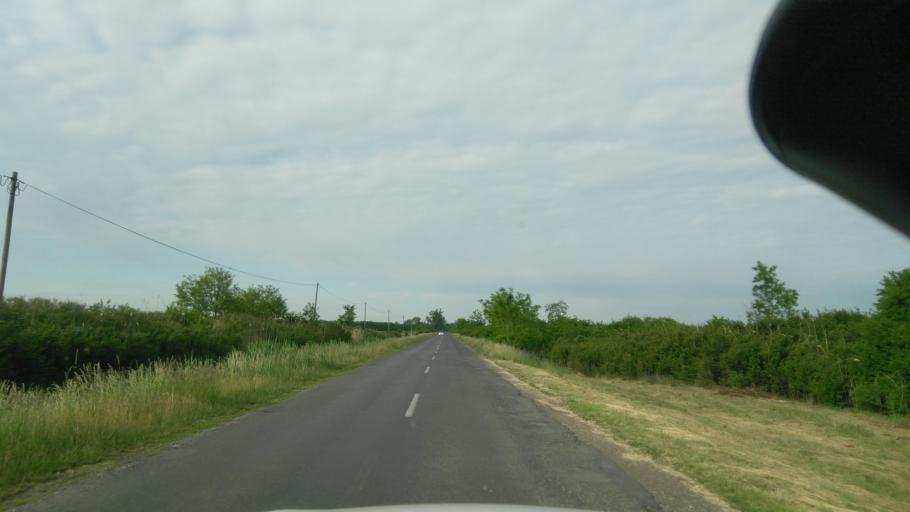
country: HU
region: Bekes
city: Elek
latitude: 46.6000
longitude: 21.2366
